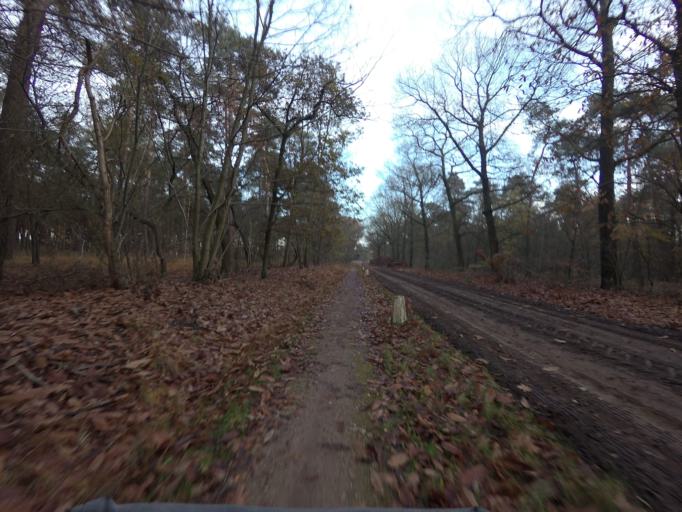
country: NL
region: North Brabant
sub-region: Gemeente Breda
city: Breda
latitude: 51.5080
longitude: 4.8134
